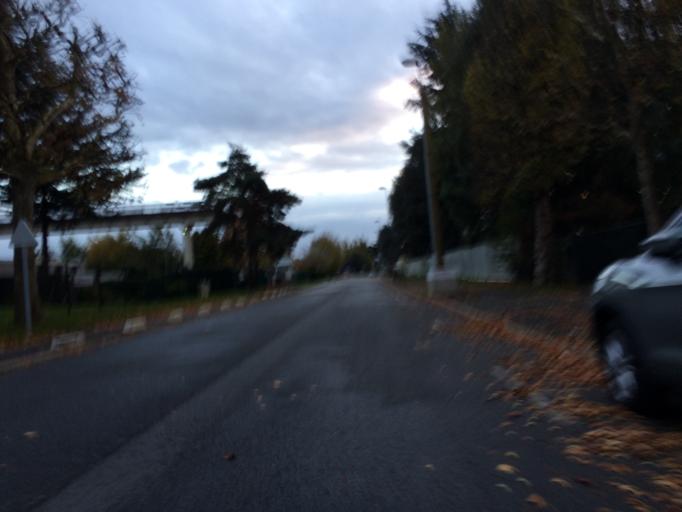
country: FR
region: Ile-de-France
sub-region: Departement de l'Essonne
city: Orsay
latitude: 48.6830
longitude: 2.1994
